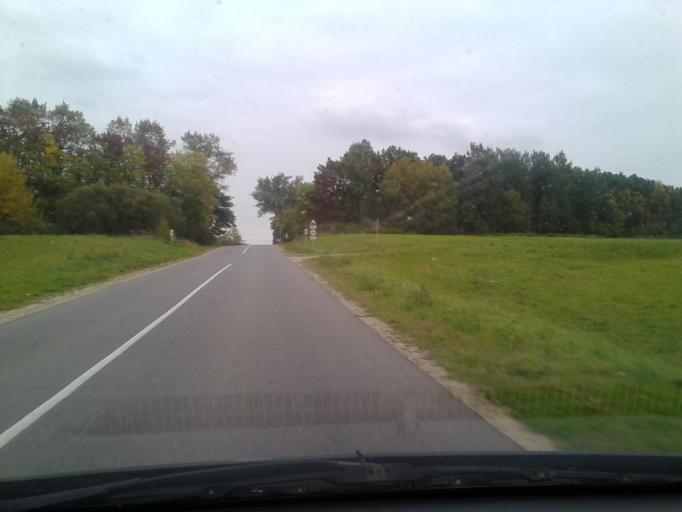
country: BY
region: Vitebsk
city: Pastavy
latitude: 55.1292
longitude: 26.9358
